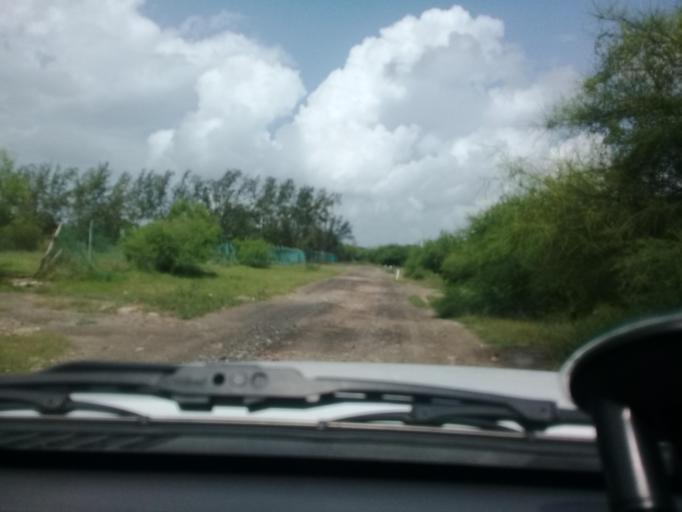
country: MX
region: Veracruz
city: Moralillo
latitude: 22.2118
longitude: -97.9571
